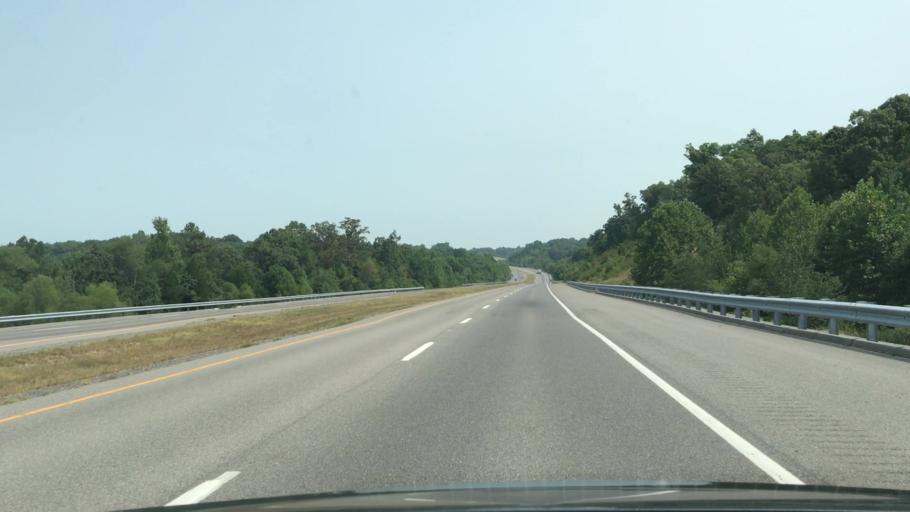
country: US
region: Kentucky
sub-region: Calloway County
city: Murray
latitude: 36.7508
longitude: -88.1570
